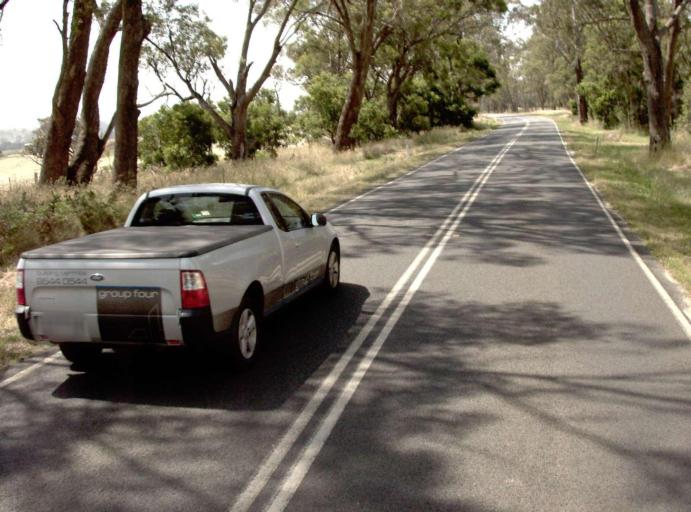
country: AU
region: Victoria
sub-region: Latrobe
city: Traralgon
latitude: -38.2693
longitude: 146.5463
